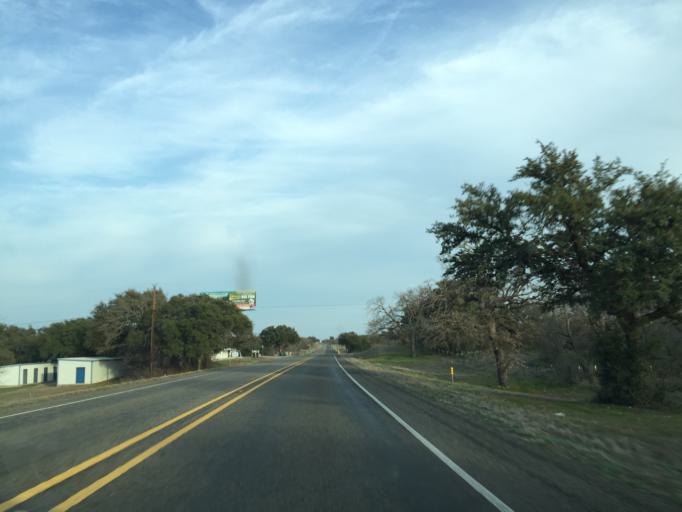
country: US
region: Texas
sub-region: Llano County
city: Llano
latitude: 30.7615
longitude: -98.6300
